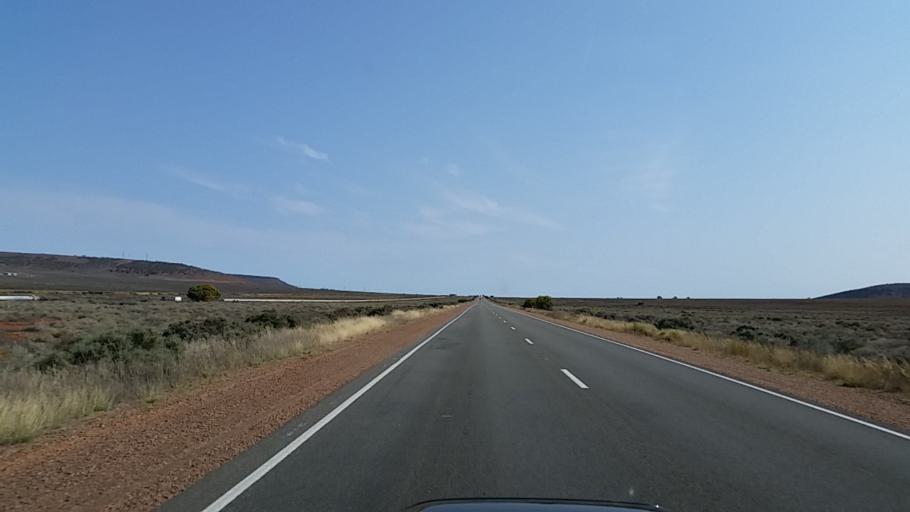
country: AU
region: South Australia
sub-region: Port Augusta
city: Port Augusta West
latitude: -32.5951
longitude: 137.6024
